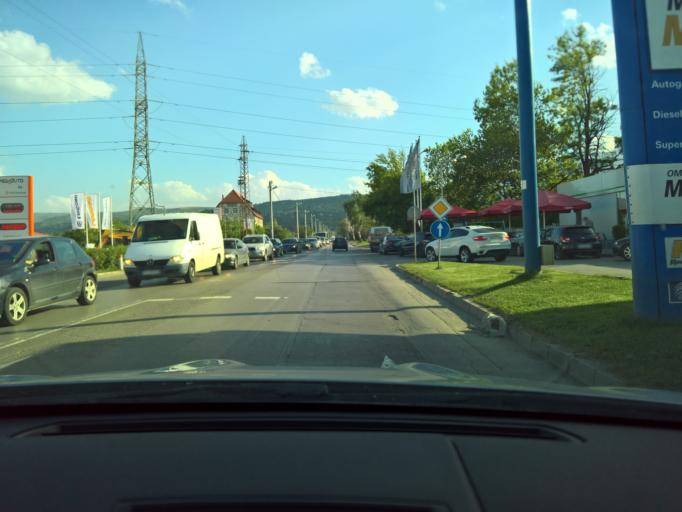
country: BG
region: Sofia-Capital
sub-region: Stolichna Obshtina
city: Sofia
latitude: 42.6206
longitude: 23.4038
